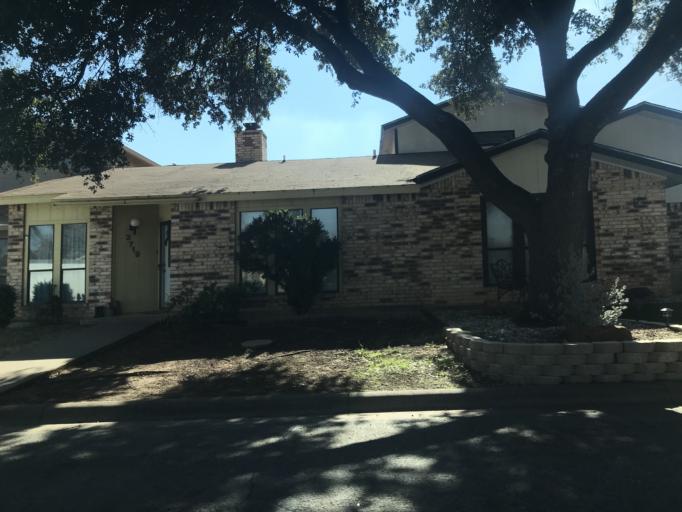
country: US
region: Texas
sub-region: Tom Green County
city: San Angelo
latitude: 31.4298
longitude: -100.4883
